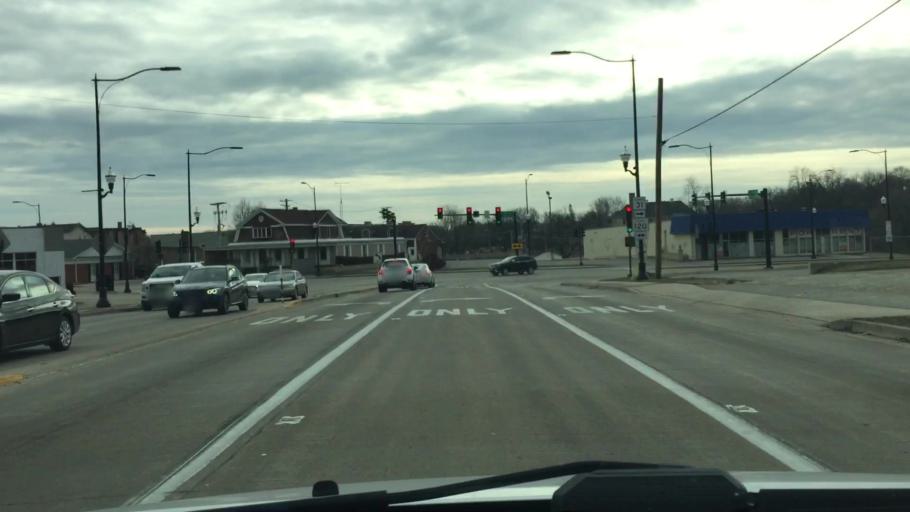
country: US
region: Illinois
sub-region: McHenry County
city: McHenry
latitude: 42.3468
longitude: -88.2674
